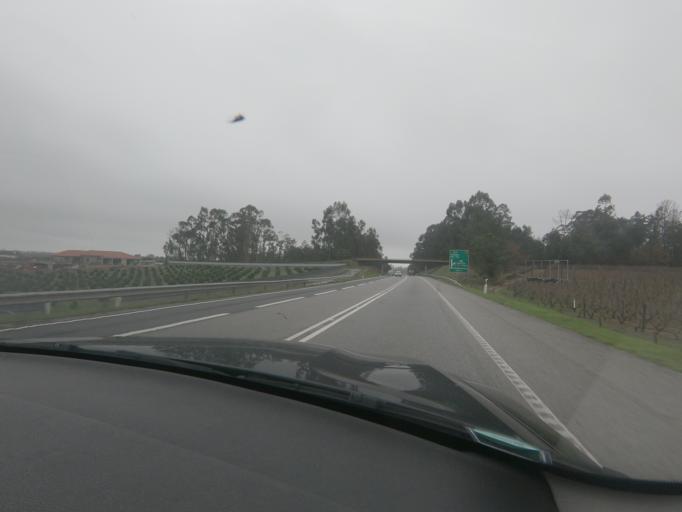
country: PT
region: Viseu
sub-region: Concelho de Tondela
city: Tondela
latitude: 40.5458
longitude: -8.0545
